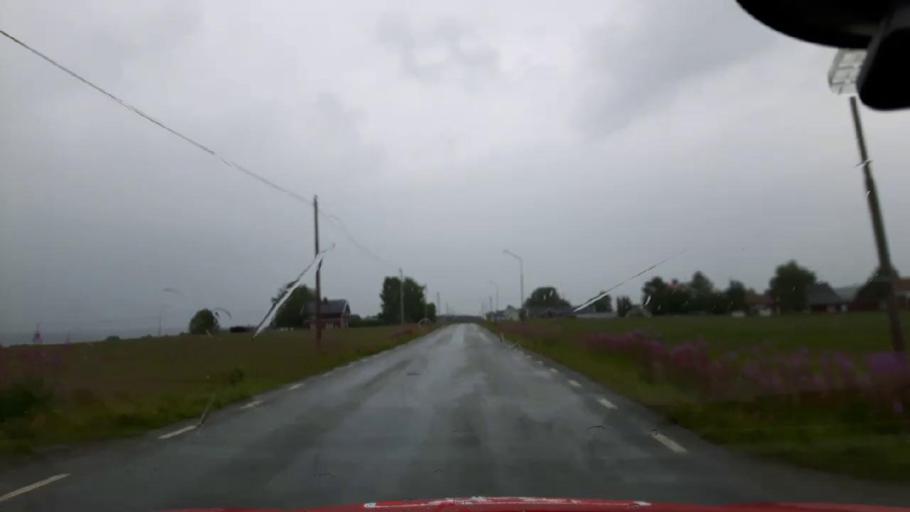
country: SE
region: Jaemtland
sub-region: OEstersunds Kommun
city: Brunflo
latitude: 62.9882
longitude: 14.8071
